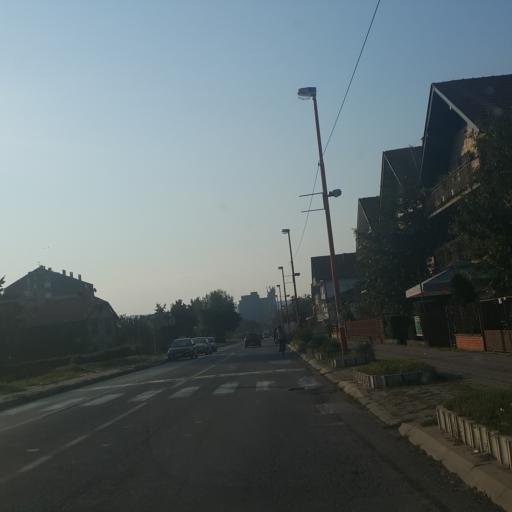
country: RS
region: Central Serbia
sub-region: Zajecarski Okrug
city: Zajecar
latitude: 43.9100
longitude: 22.2609
